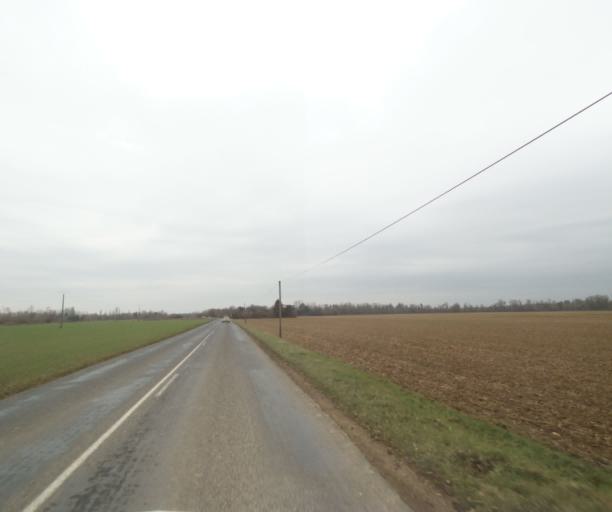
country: FR
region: Champagne-Ardenne
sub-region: Departement de la Haute-Marne
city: Villiers-en-Lieu
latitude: 48.6551
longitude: 4.9089
